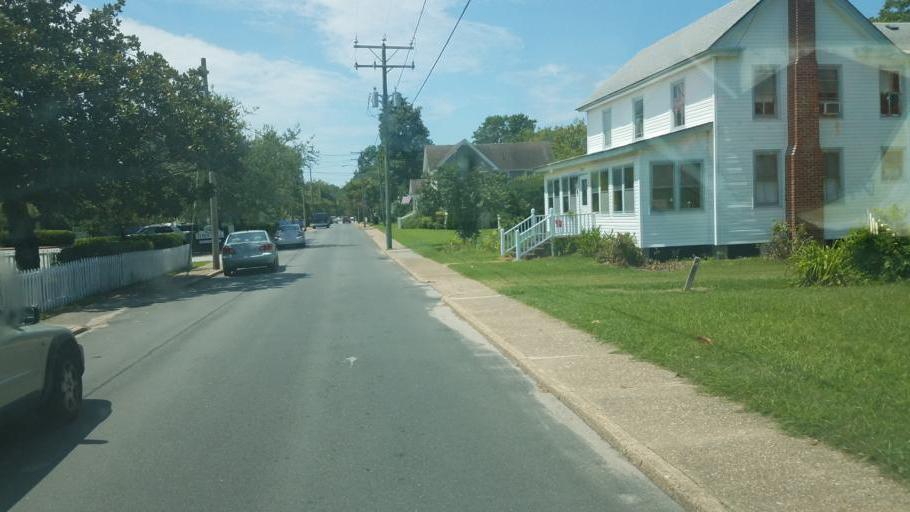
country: US
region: North Carolina
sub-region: Dare County
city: Manteo
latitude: 35.9094
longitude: -75.6739
